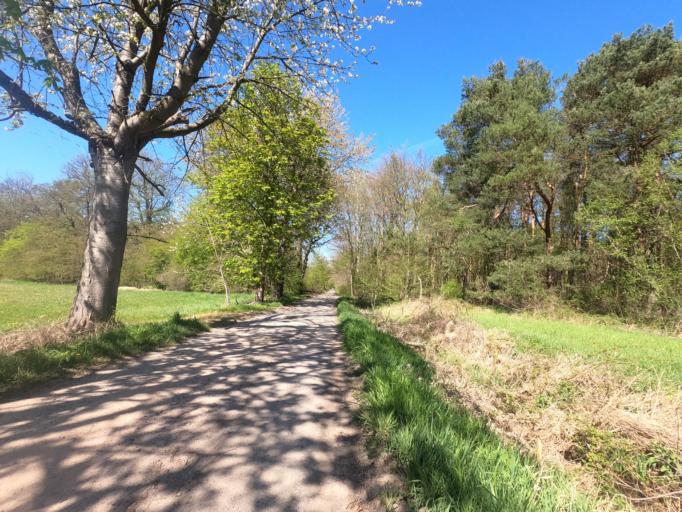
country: DE
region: Hesse
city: Morfelden-Walldorf
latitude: 49.9597
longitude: 8.5939
